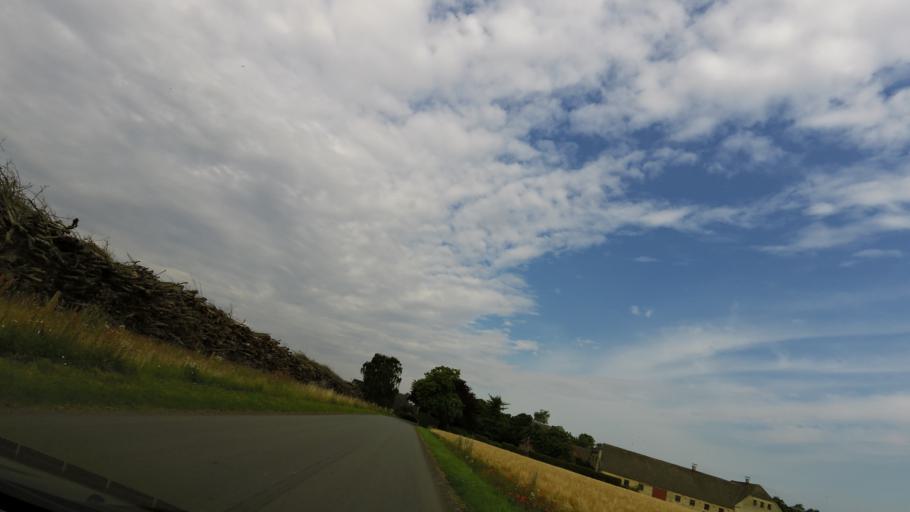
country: DK
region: South Denmark
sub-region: Nordfyns Kommune
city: Otterup
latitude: 55.5560
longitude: 10.4179
